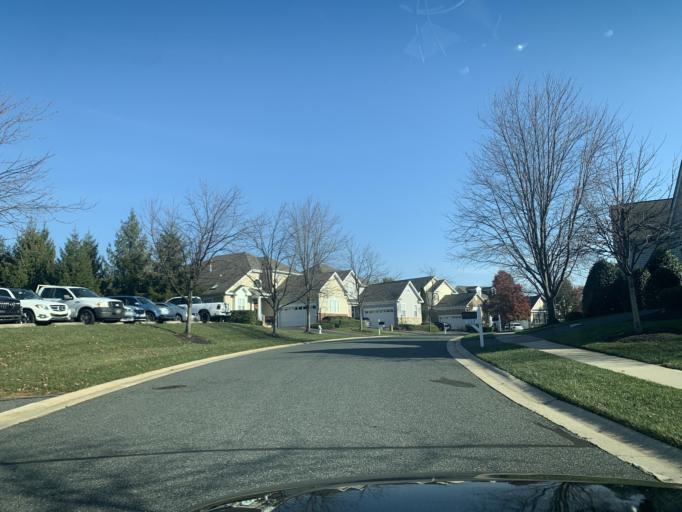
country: US
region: Maryland
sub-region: Harford County
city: Havre de Grace
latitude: 39.5490
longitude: -76.1279
